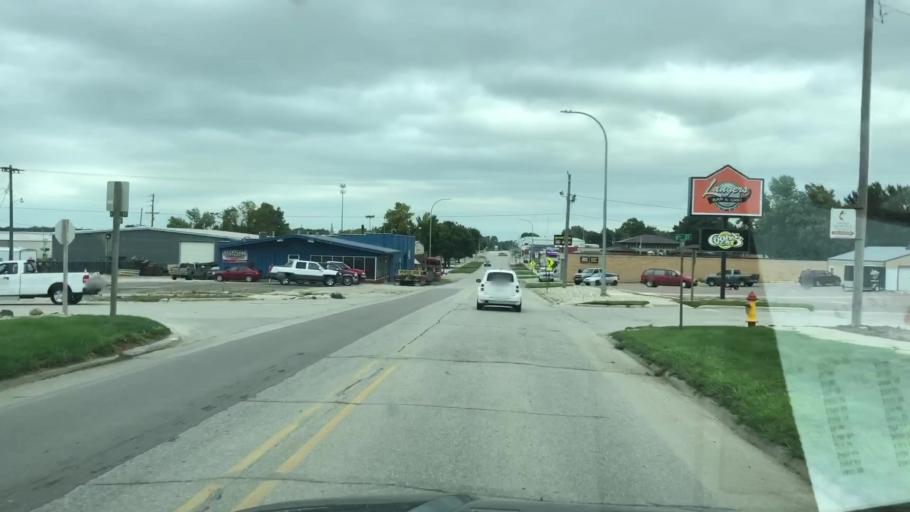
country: US
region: Iowa
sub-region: O'Brien County
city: Sheldon
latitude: 43.1820
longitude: -95.8558
